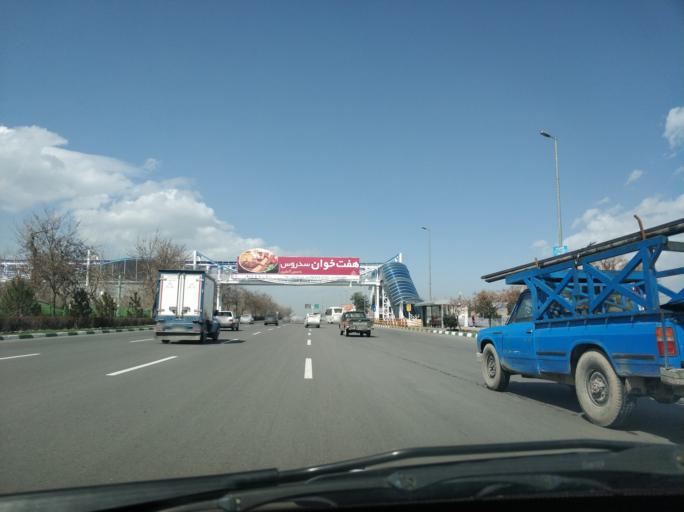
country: IR
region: Razavi Khorasan
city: Torqabeh
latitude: 36.3410
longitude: 59.4590
